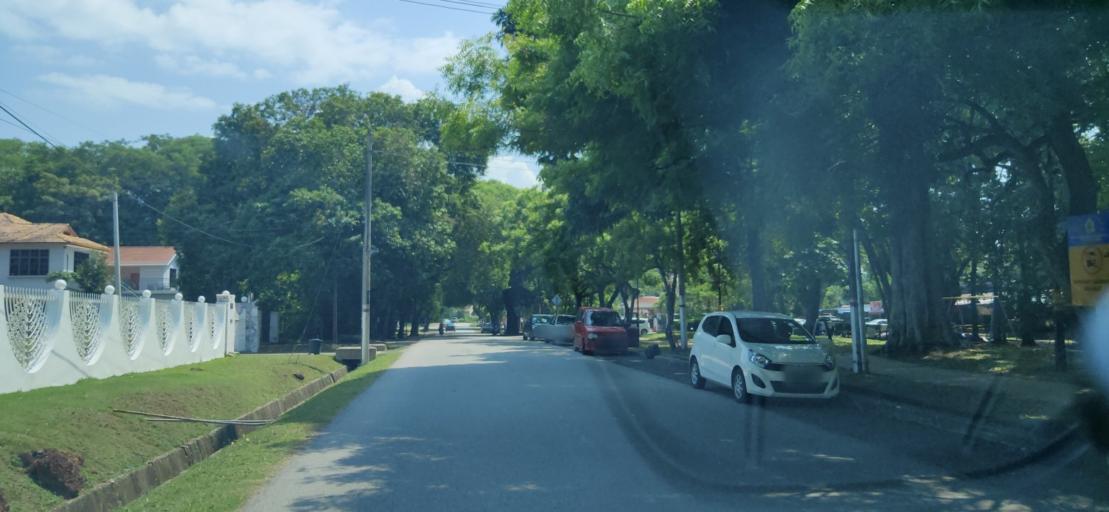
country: MY
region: Kedah
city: Sungai Petani
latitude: 5.6468
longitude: 100.4841
